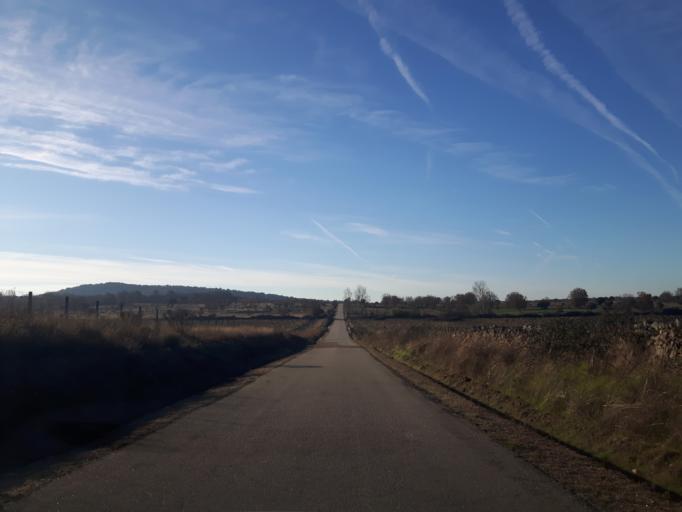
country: ES
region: Castille and Leon
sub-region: Provincia de Salamanca
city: Olmedo de Camaces
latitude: 40.9176
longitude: -6.6169
